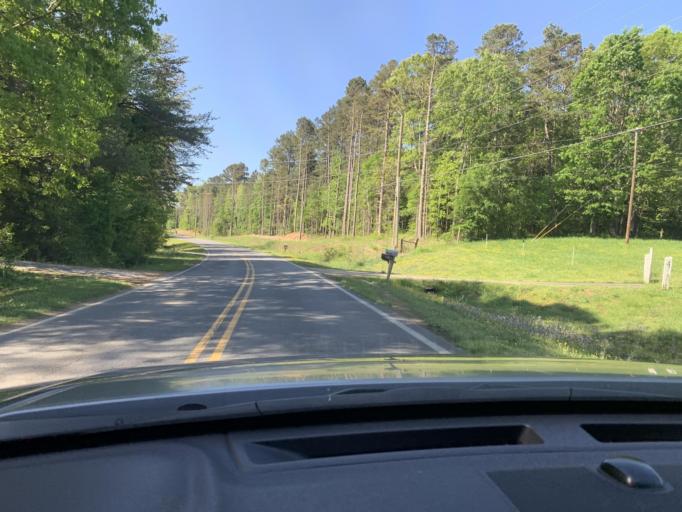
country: US
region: Georgia
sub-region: Polk County
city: Cedartown
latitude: 34.0226
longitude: -85.3027
